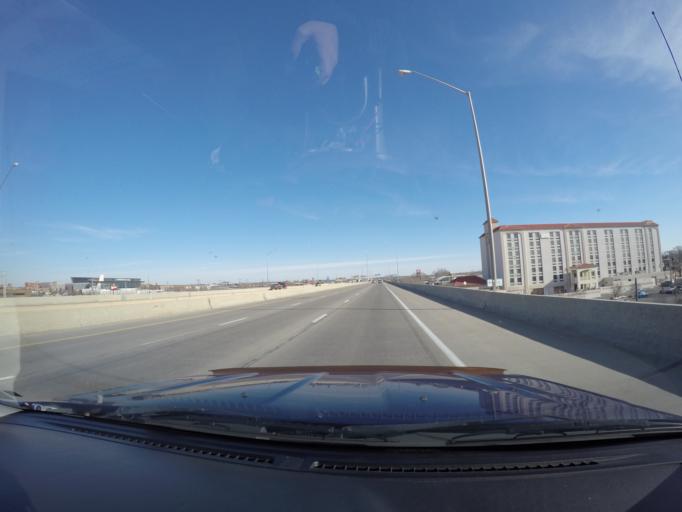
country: US
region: Kansas
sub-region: Sedgwick County
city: Wichita
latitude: 37.6788
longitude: -97.3367
